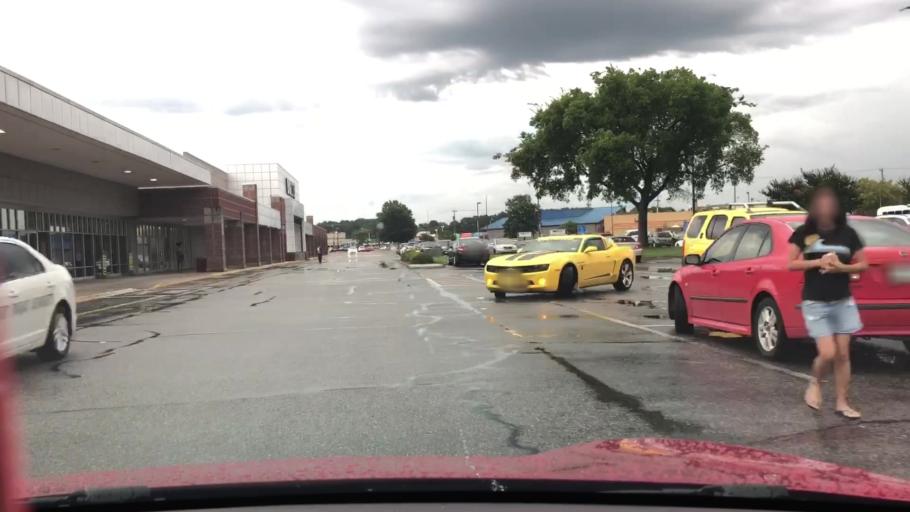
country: US
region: Virginia
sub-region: City of Chesapeake
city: Chesapeake
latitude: 36.8578
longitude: -76.2036
